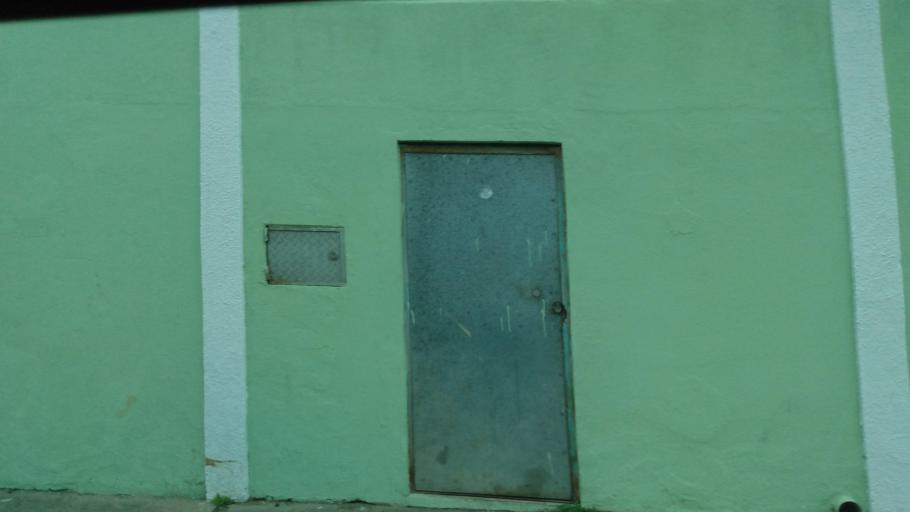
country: BR
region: Pernambuco
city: Garanhuns
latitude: -8.8914
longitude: -36.4907
